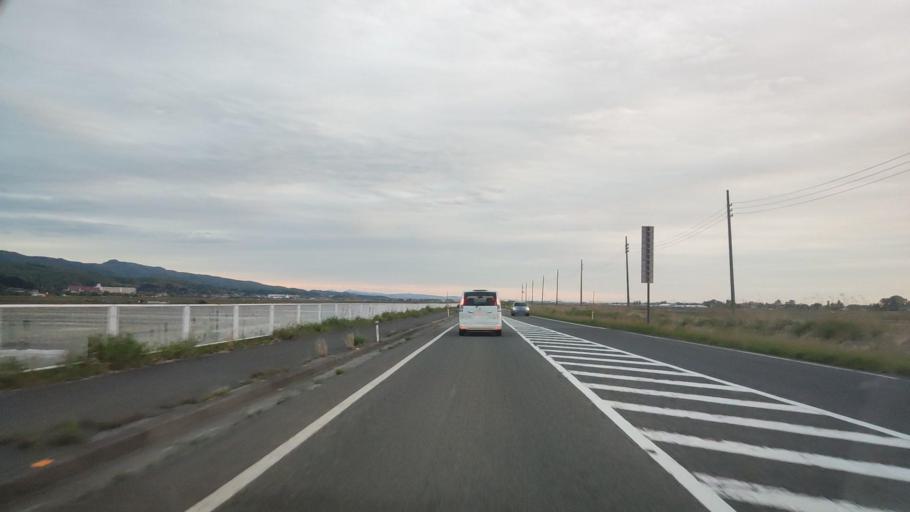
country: JP
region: Niigata
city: Niitsu-honcho
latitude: 37.7704
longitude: 139.1023
